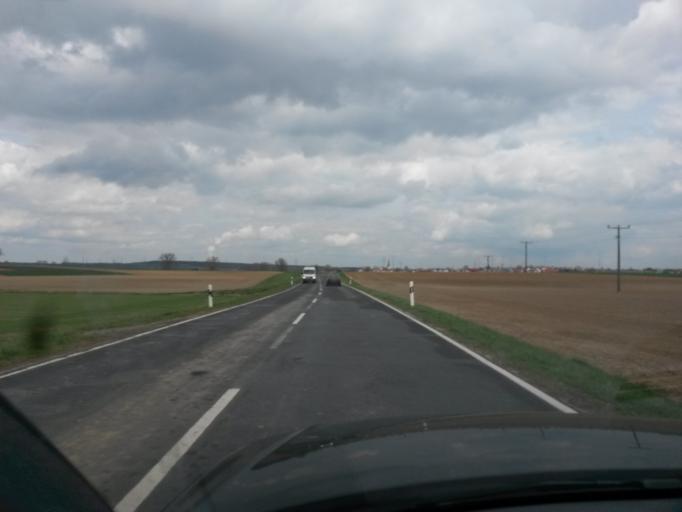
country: DE
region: Bavaria
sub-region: Regierungsbezirk Unterfranken
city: Oberpleichfeld
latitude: 49.8709
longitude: 10.0702
